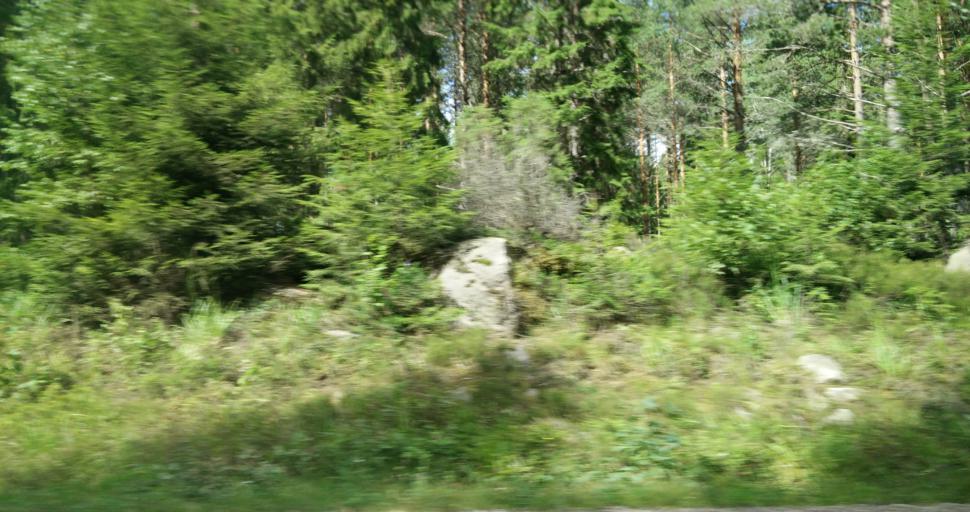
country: SE
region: Vaermland
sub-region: Hagfors Kommun
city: Ekshaerad
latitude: 60.0903
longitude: 13.4494
